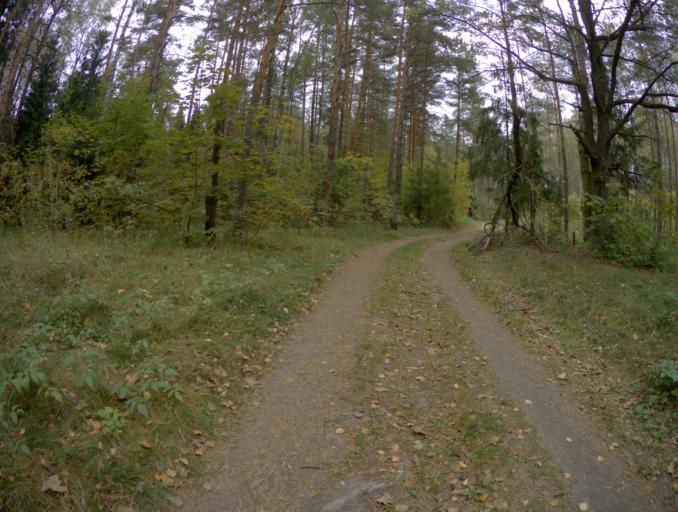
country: RU
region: Vladimir
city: Bogolyubovo
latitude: 56.1240
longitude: 40.5372
